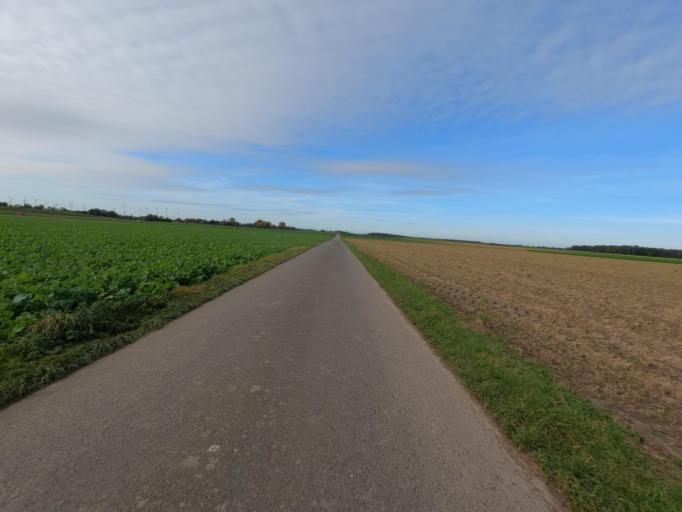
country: DE
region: North Rhine-Westphalia
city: Erkelenz
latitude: 51.0423
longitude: 6.3482
